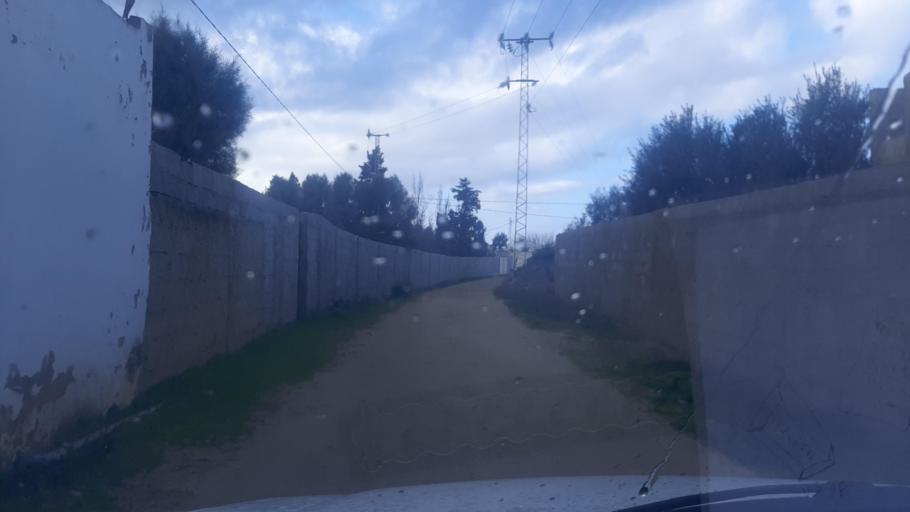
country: TN
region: Nabul
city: Manzil Bu Zalafah
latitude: 36.7421
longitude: 10.5278
